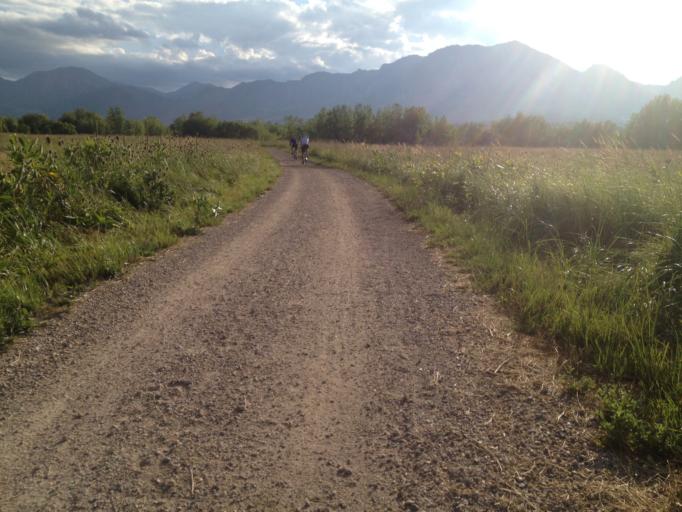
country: US
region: Colorado
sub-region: Boulder County
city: Superior
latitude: 39.9711
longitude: -105.2260
